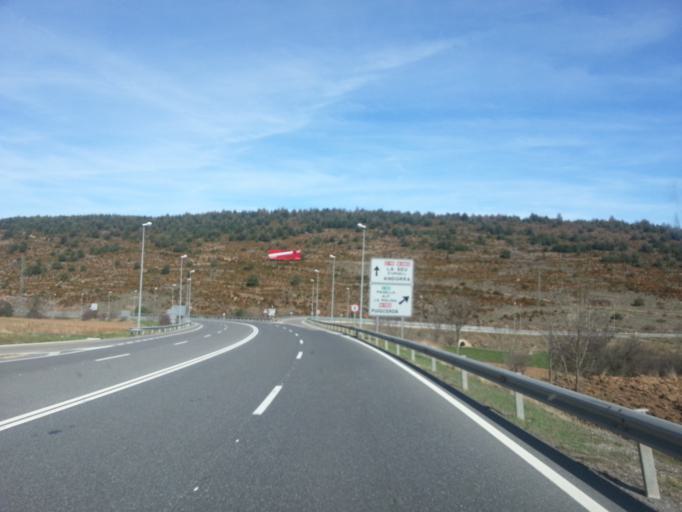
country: ES
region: Catalonia
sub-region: Provincia de Lleida
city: Riu de Cerdanya
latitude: 42.3472
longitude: 1.8332
